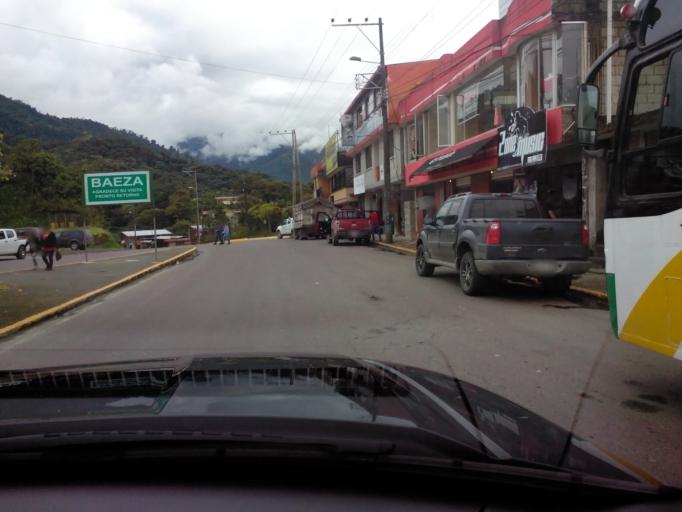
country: EC
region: Napo
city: Archidona
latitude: -0.4645
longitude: -77.8917
